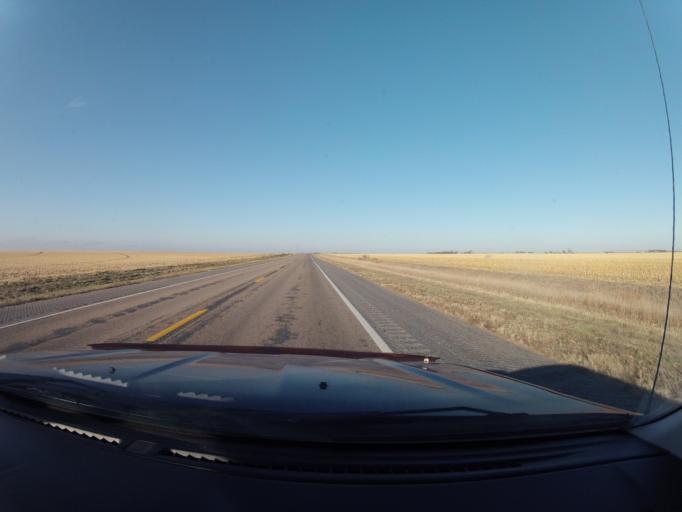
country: US
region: Nebraska
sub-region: Kearney County
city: Minden
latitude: 40.5543
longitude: -98.9518
